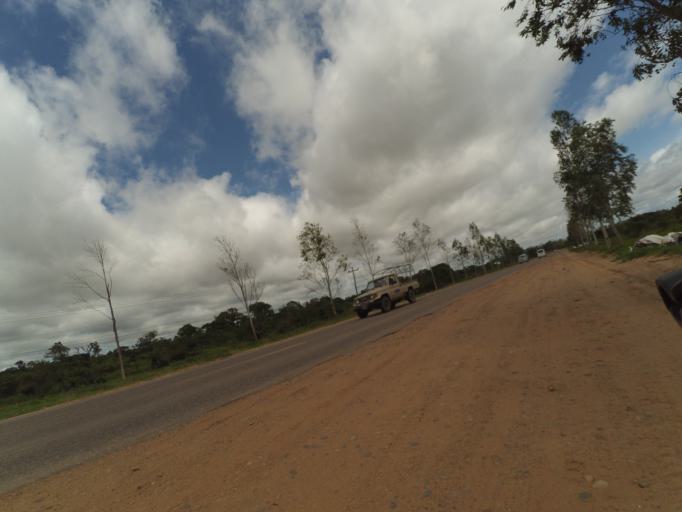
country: BO
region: Santa Cruz
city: Santa Rita
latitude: -17.9113
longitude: -63.2509
